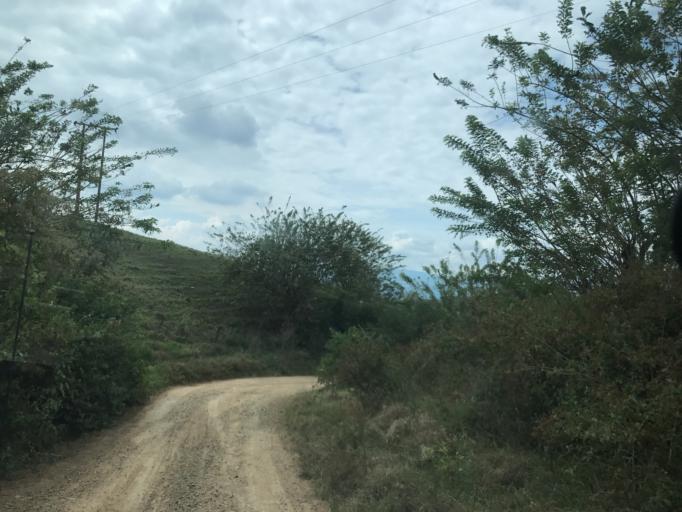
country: CO
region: Valle del Cauca
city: Obando
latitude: 4.5584
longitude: -75.9451
